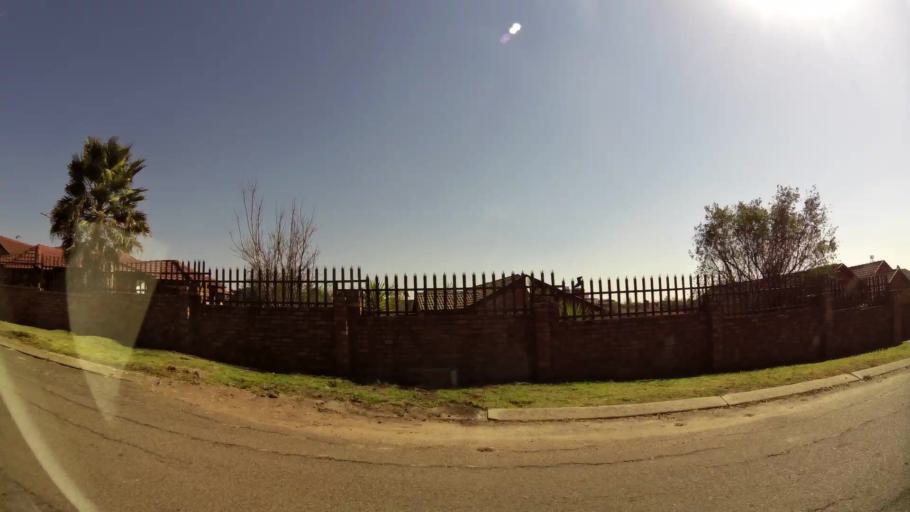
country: ZA
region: Gauteng
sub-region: City of Johannesburg Metropolitan Municipality
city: Modderfontein
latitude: -26.0676
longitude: 28.1969
